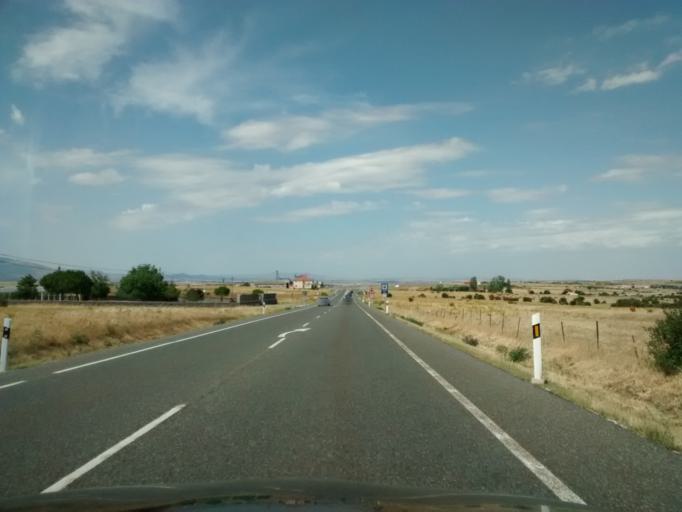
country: ES
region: Castille and Leon
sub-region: Provincia de Segovia
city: Torrecaballeros
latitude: 40.9901
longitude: -4.0329
